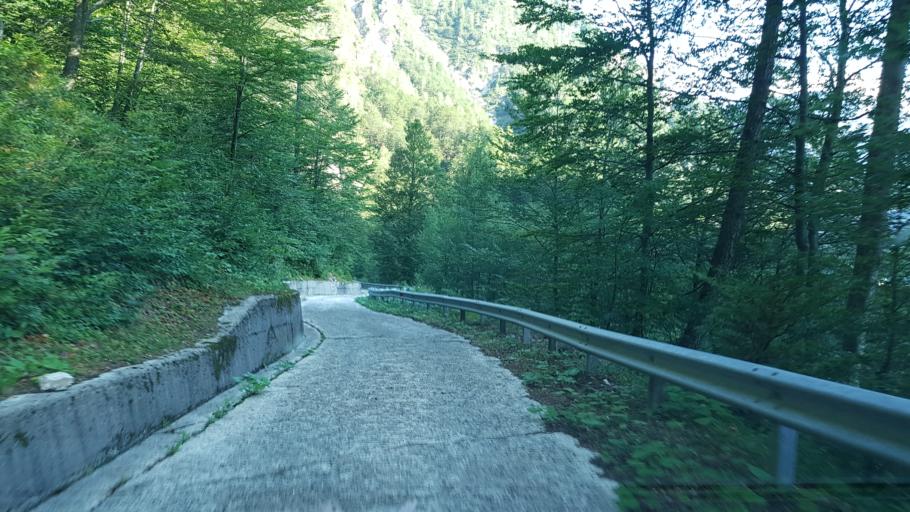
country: IT
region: Friuli Venezia Giulia
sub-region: Provincia di Udine
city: Pontebba
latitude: 46.4796
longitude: 13.2517
